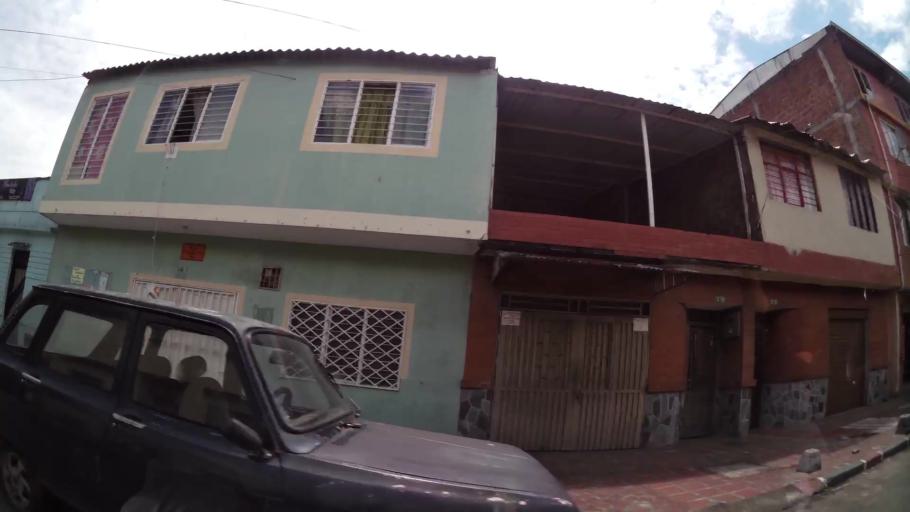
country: CO
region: Valle del Cauca
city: Cali
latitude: 3.4401
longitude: -76.5111
